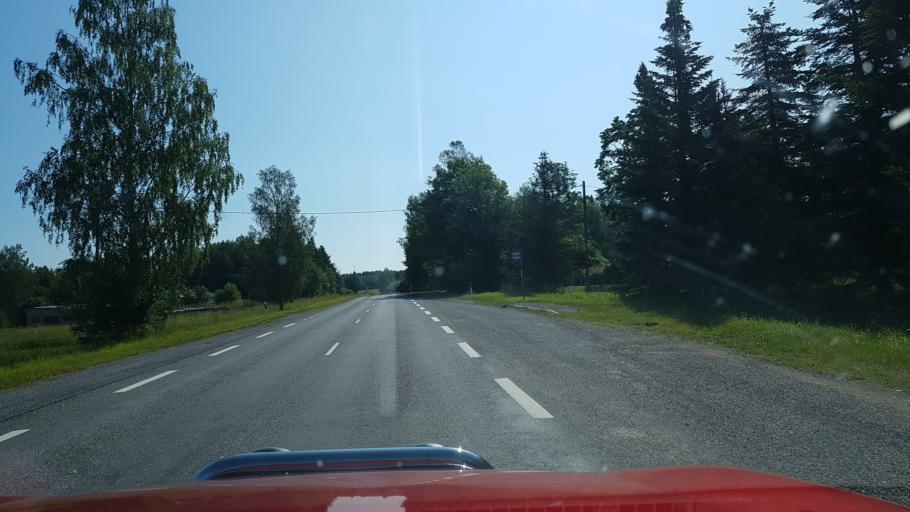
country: EE
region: Vorumaa
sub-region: Voru linn
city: Voru
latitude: 57.9741
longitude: 26.8364
